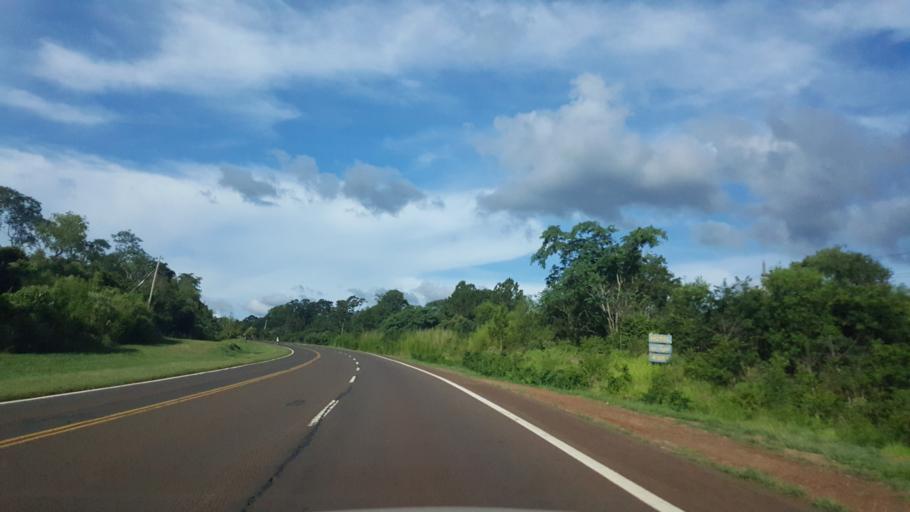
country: AR
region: Misiones
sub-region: Departamento de Candelaria
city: Loreto
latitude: -27.3528
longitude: -55.5501
